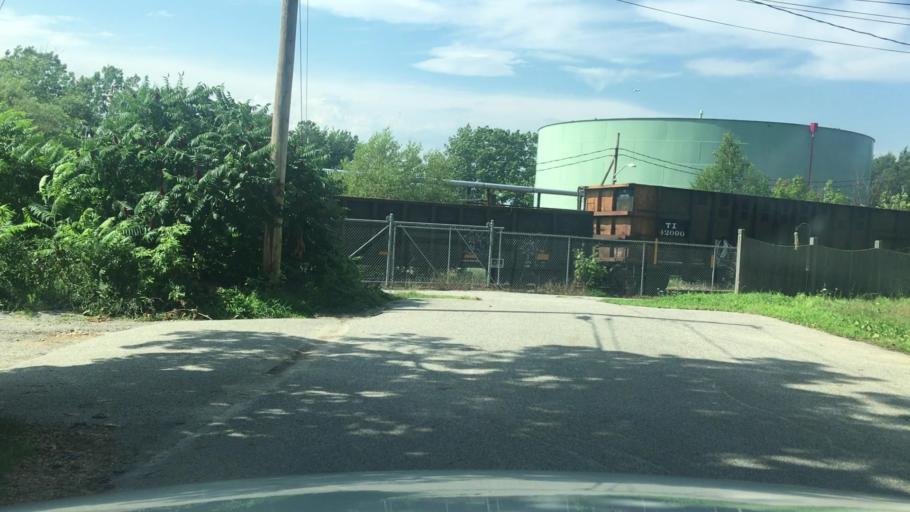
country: US
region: Maine
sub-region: Cumberland County
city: South Portland
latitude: 43.6326
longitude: -70.2723
